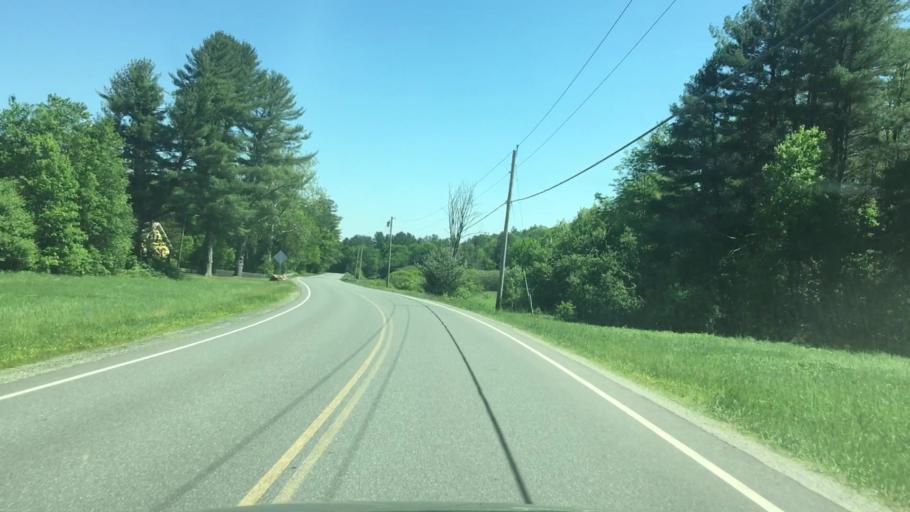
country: US
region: Massachusetts
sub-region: Franklin County
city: Colrain
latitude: 42.7250
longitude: -72.7131
